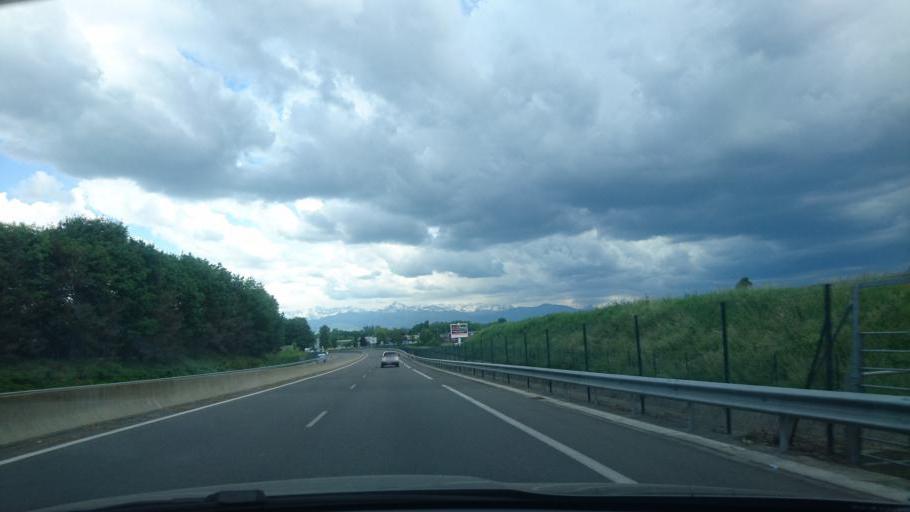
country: FR
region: Midi-Pyrenees
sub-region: Departement des Hautes-Pyrenees
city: Odos
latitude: 43.2264
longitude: 0.0451
